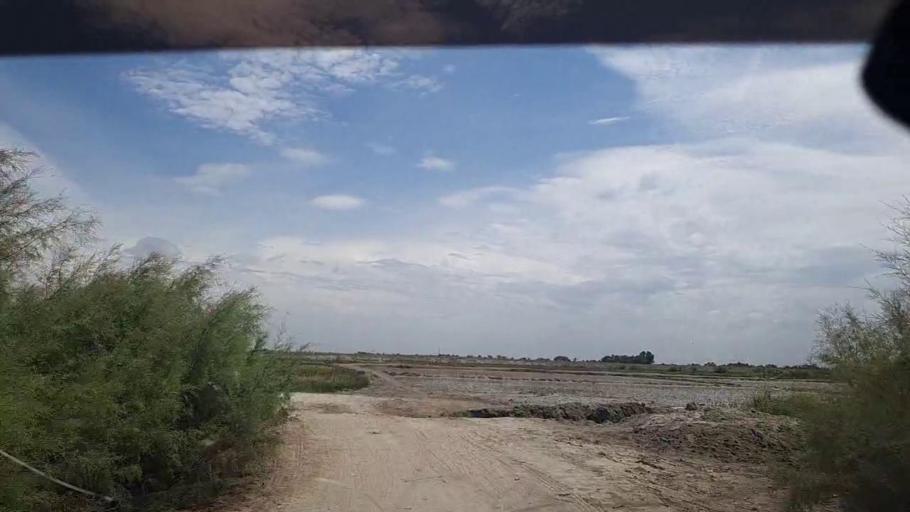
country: PK
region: Sindh
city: Ghauspur
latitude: 28.1439
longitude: 68.9780
